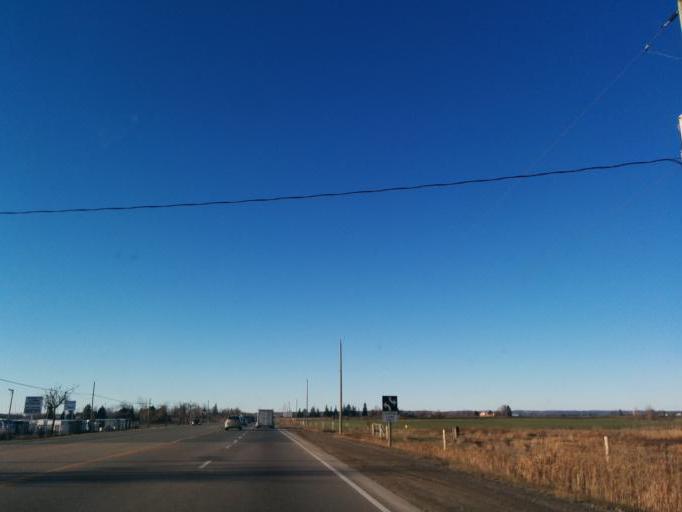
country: CA
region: Ontario
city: Brampton
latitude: 43.7742
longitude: -79.8791
